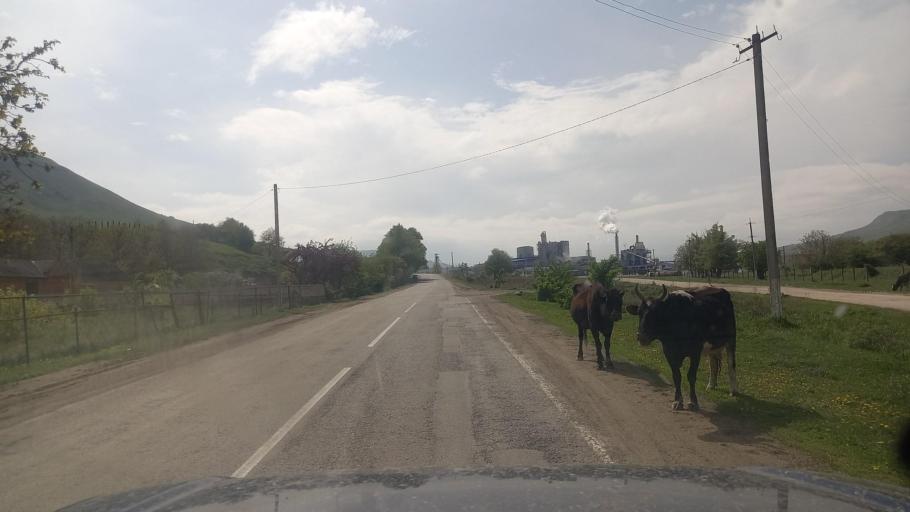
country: RU
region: Kabardino-Balkariya
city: Sarmakovo
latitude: 43.7284
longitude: 43.1511
